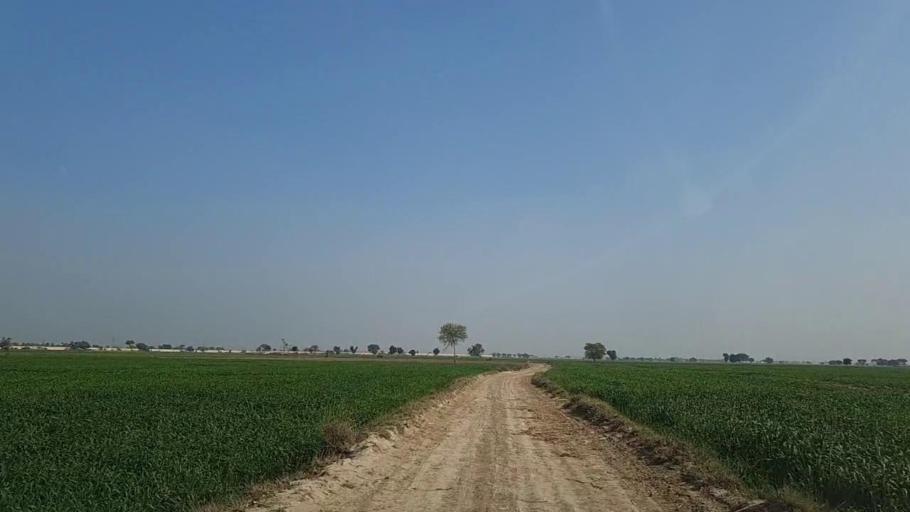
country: PK
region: Sindh
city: Moro
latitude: 26.6813
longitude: 67.9314
